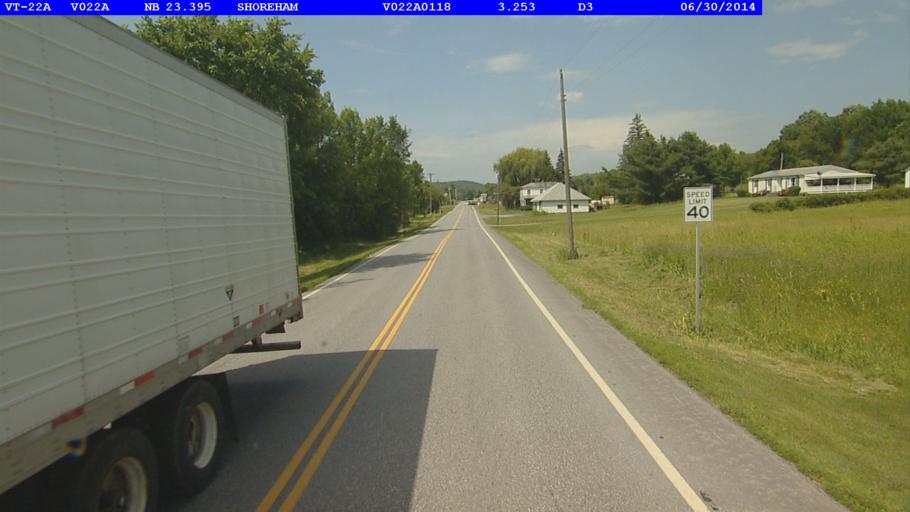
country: US
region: New York
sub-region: Essex County
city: Ticonderoga
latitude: 43.8964
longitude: -73.3088
